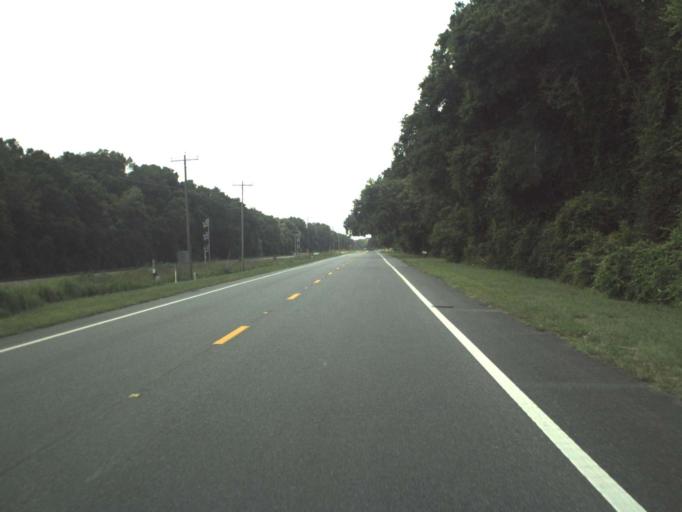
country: US
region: Florida
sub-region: Sumter County
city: Bushnell
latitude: 28.5947
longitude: -82.1460
